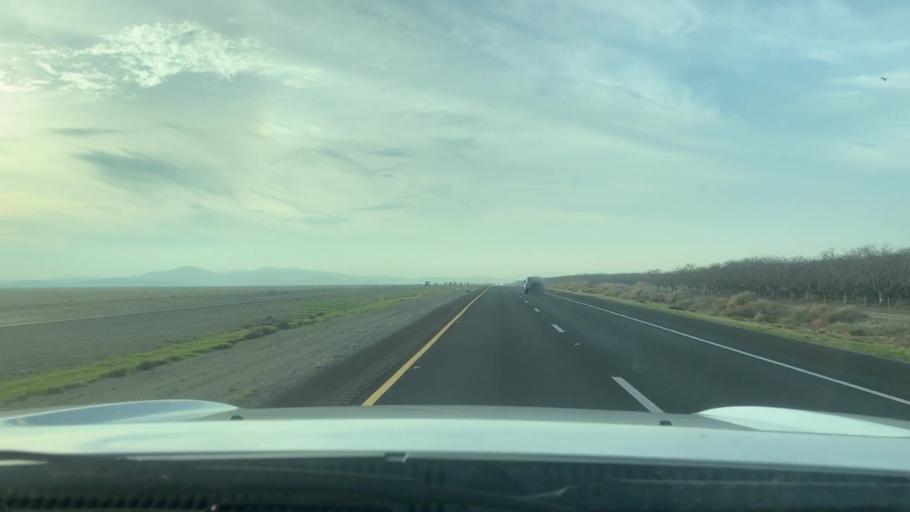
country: US
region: California
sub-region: Kern County
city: Lost Hills
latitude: 35.6146
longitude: -119.9374
